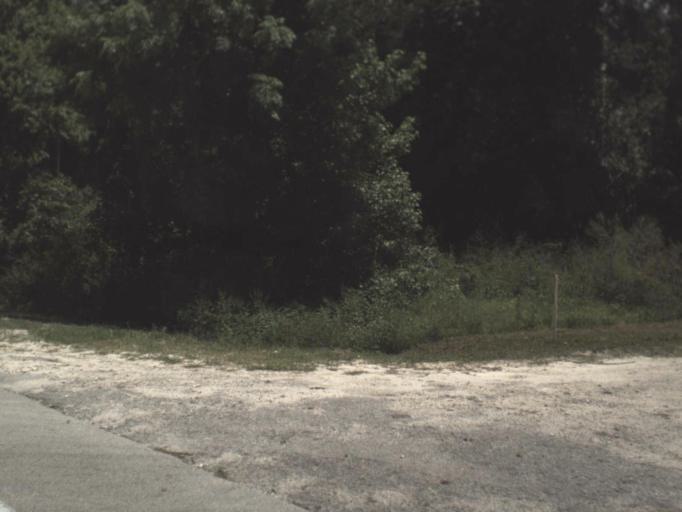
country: US
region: Florida
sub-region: Putnam County
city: Crescent City
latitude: 29.4120
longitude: -81.5097
